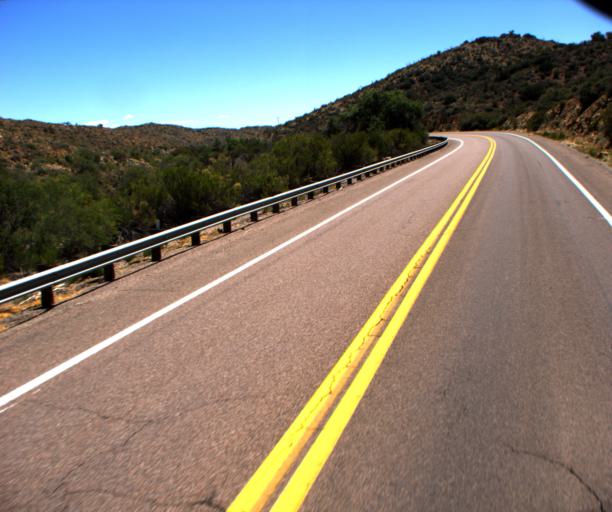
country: US
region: Arizona
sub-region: Yavapai County
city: Bagdad
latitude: 34.5592
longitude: -113.1636
